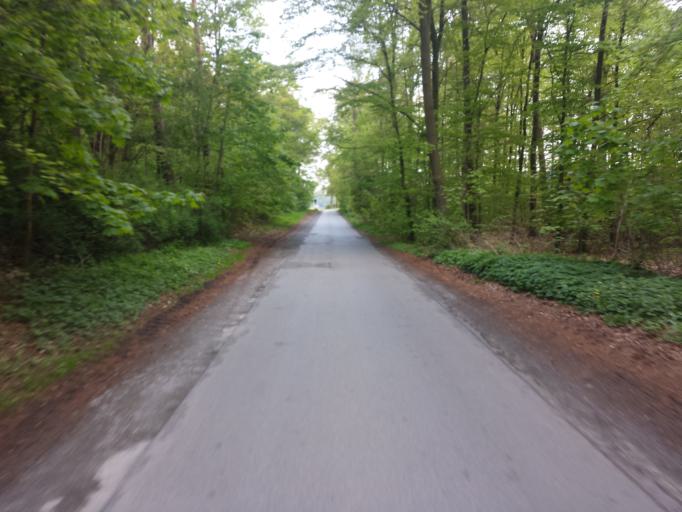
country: DE
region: North Rhine-Westphalia
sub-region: Regierungsbezirk Detmold
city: Guetersloh
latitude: 51.8925
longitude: 8.3454
